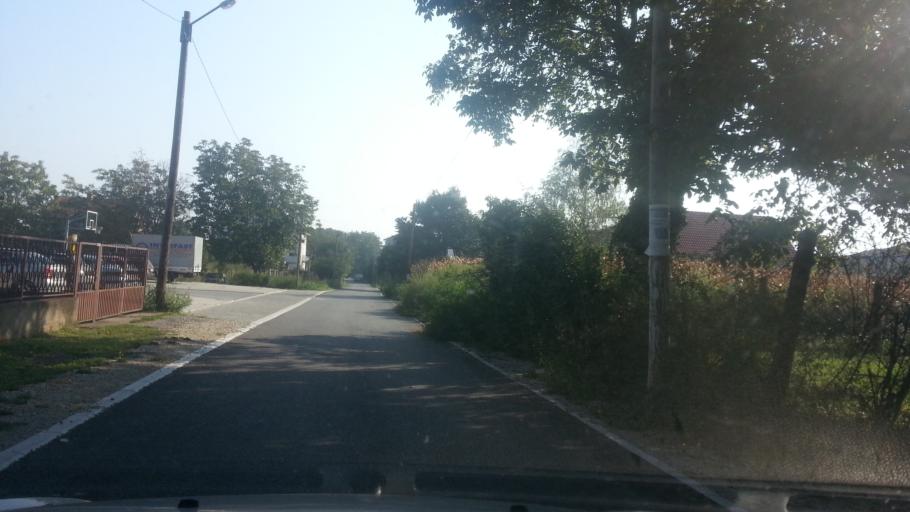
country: RS
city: Novi Banovci
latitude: 44.9449
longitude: 20.2849
